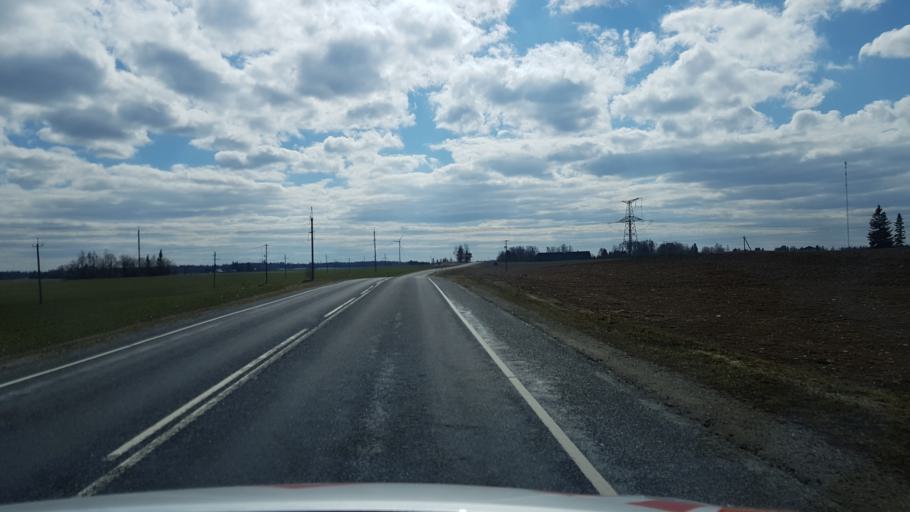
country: EE
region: Laeaene-Virumaa
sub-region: Vaeike-Maarja vald
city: Vaike-Maarja
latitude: 59.2197
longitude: 26.2683
